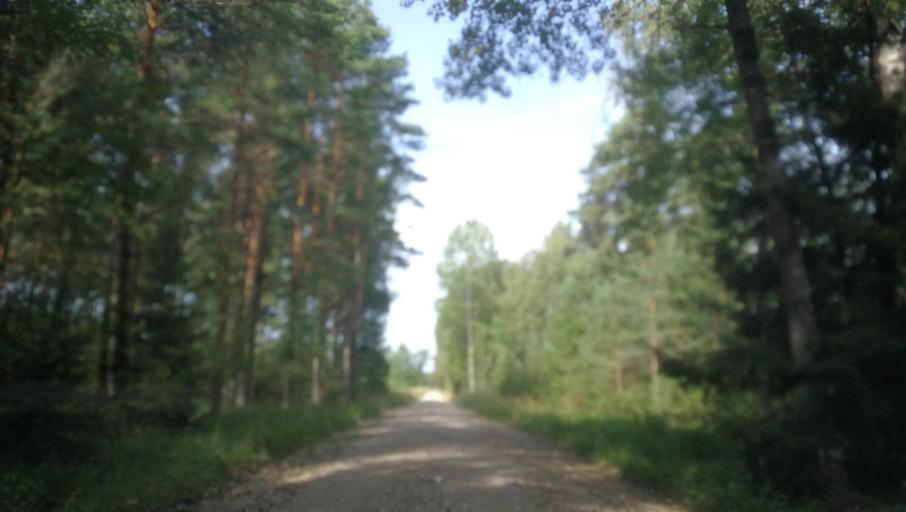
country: LV
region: Pavilostas
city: Pavilosta
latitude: 56.8334
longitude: 21.2839
